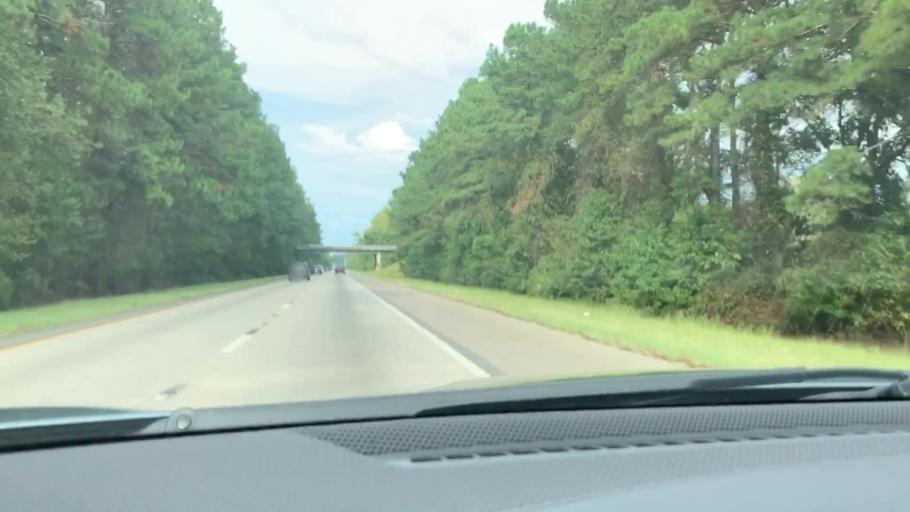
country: US
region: South Carolina
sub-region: Colleton County
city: Walterboro
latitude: 32.8939
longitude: -80.7102
